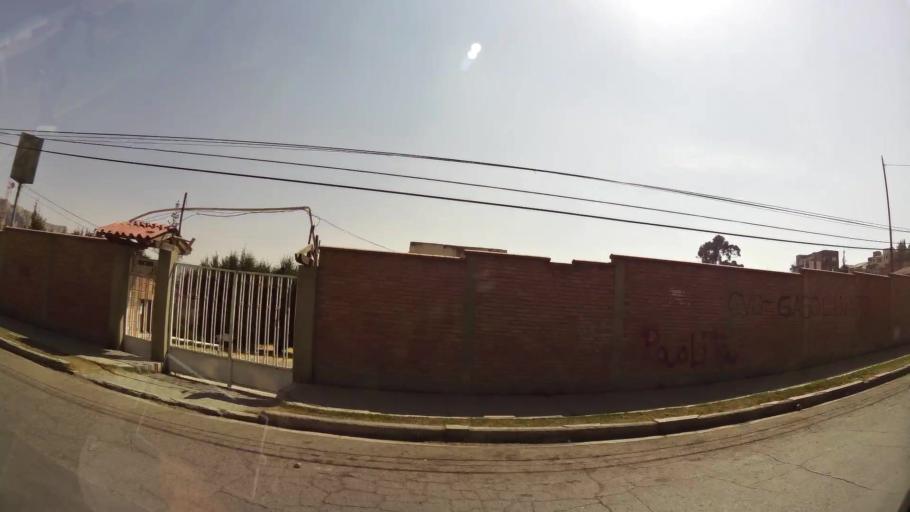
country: BO
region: La Paz
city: La Paz
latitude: -16.5449
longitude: -68.0638
